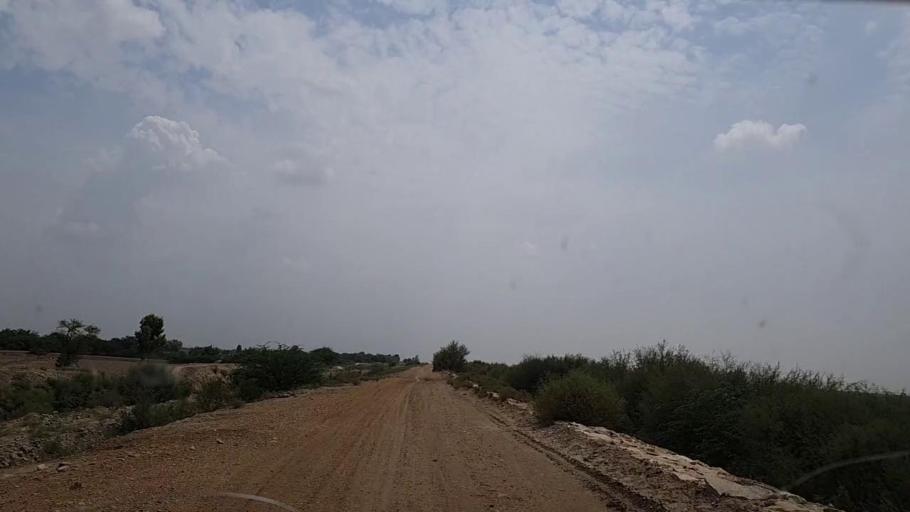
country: PK
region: Sindh
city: Phulji
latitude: 26.8136
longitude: 67.6085
